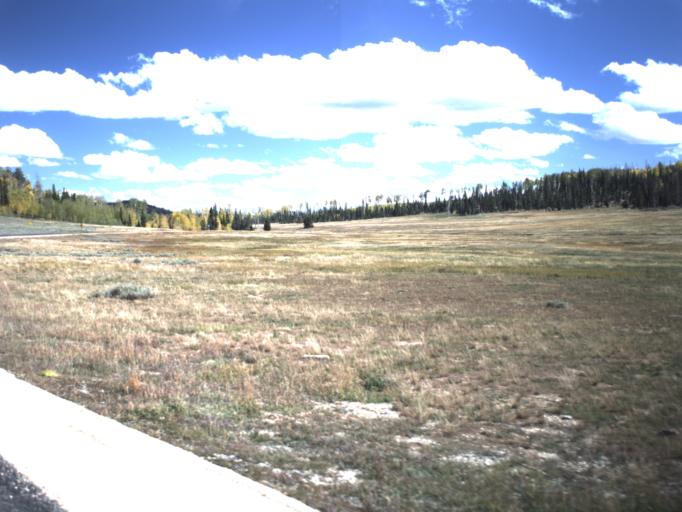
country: US
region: Utah
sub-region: Iron County
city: Parowan
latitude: 37.5712
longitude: -112.8106
